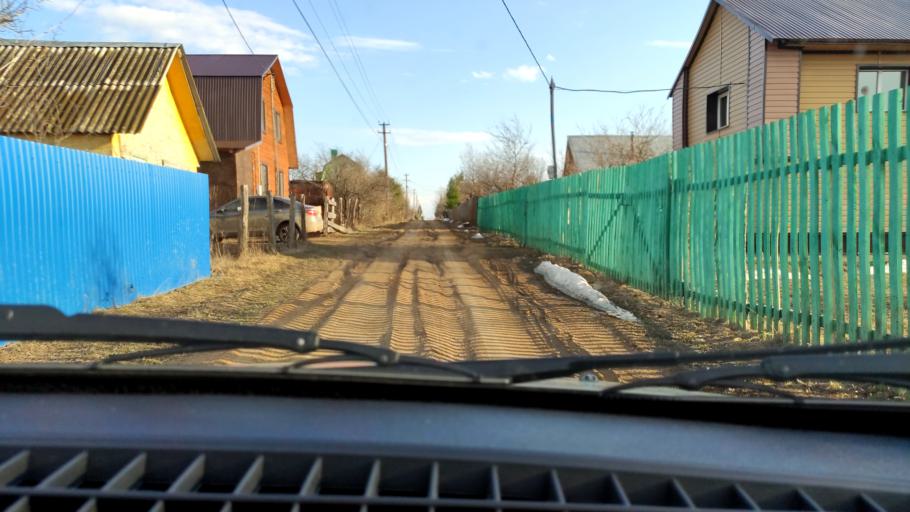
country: RU
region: Bashkortostan
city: Iglino
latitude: 54.8441
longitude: 56.4711
